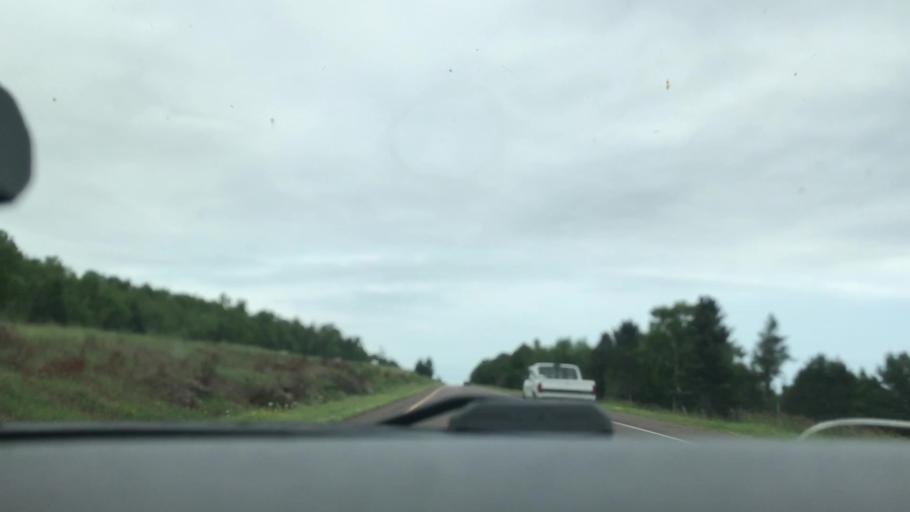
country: US
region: Minnesota
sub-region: Lake County
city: Two Harbors
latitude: 46.9823
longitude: -91.7444
